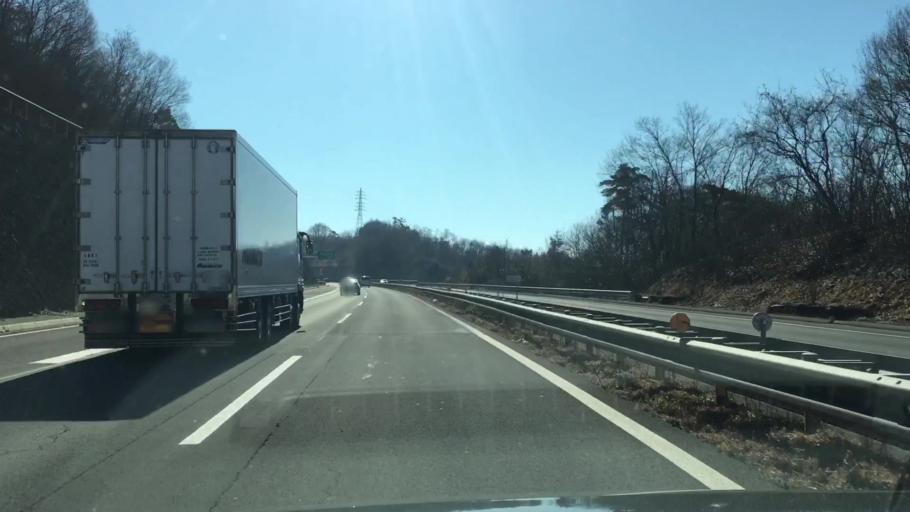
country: JP
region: Nagano
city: Ueda
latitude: 36.3933
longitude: 138.3130
